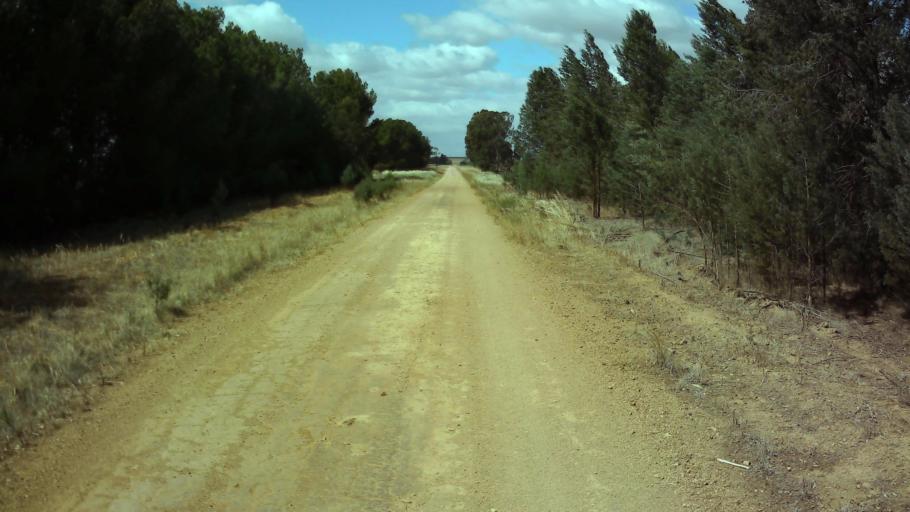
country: AU
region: New South Wales
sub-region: Weddin
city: Grenfell
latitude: -34.0482
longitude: 148.3325
